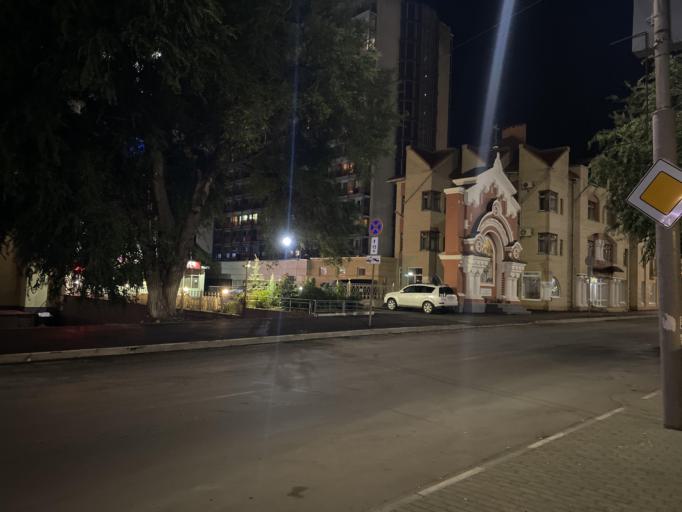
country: RU
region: Saratov
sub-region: Saratovskiy Rayon
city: Saratov
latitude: 51.5274
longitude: 46.0543
